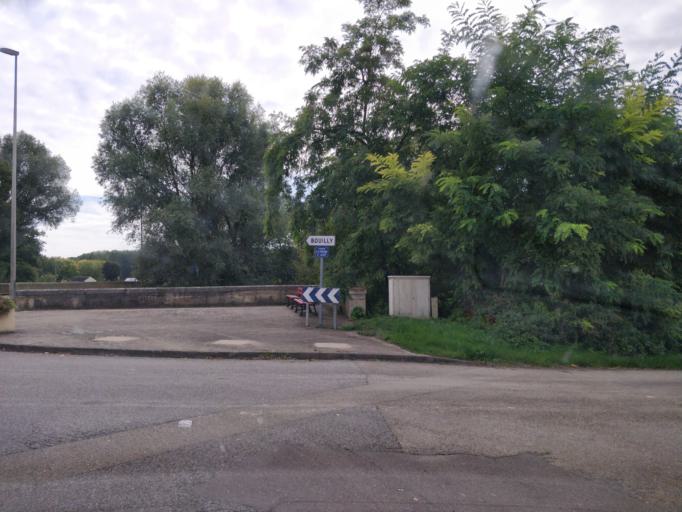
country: FR
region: Bourgogne
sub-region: Departement de l'Yonne
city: Brienon-sur-Armancon
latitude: 47.9859
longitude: 3.6131
